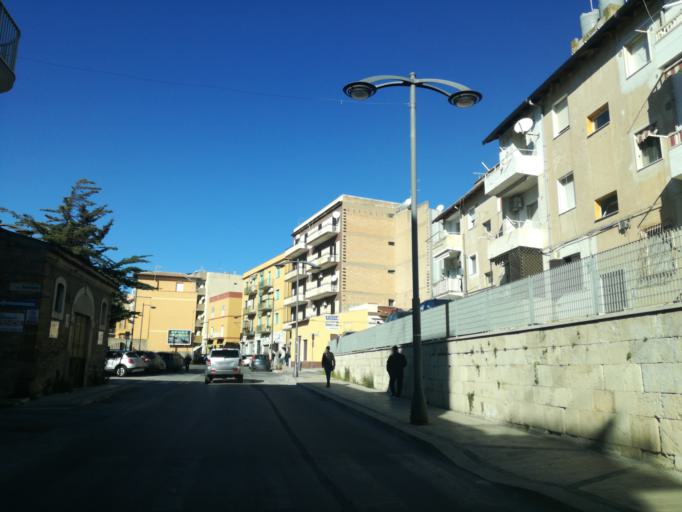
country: IT
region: Sicily
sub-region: Provincia di Caltanissetta
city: Gela
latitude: 37.0724
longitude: 14.2351
